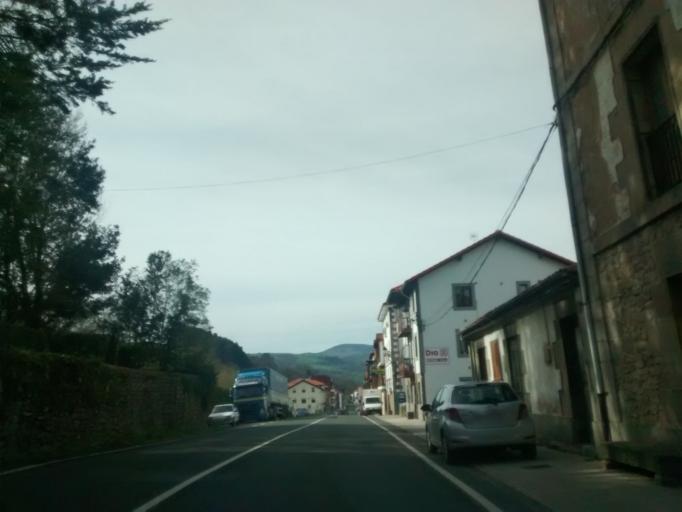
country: ES
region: Cantabria
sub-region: Provincia de Cantabria
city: Santiurde de Toranzo
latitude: 43.1946
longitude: -3.9195
